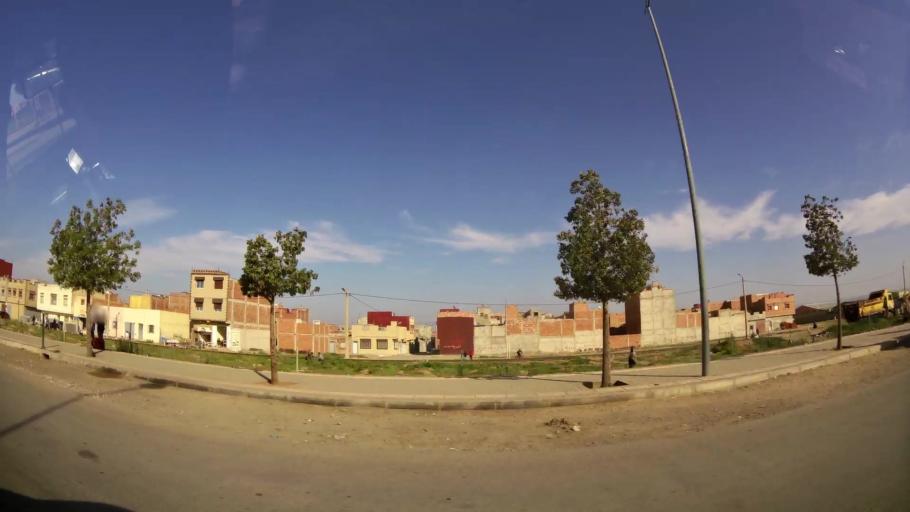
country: MA
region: Oriental
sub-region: Oujda-Angad
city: Oujda
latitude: 34.7120
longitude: -1.8882
